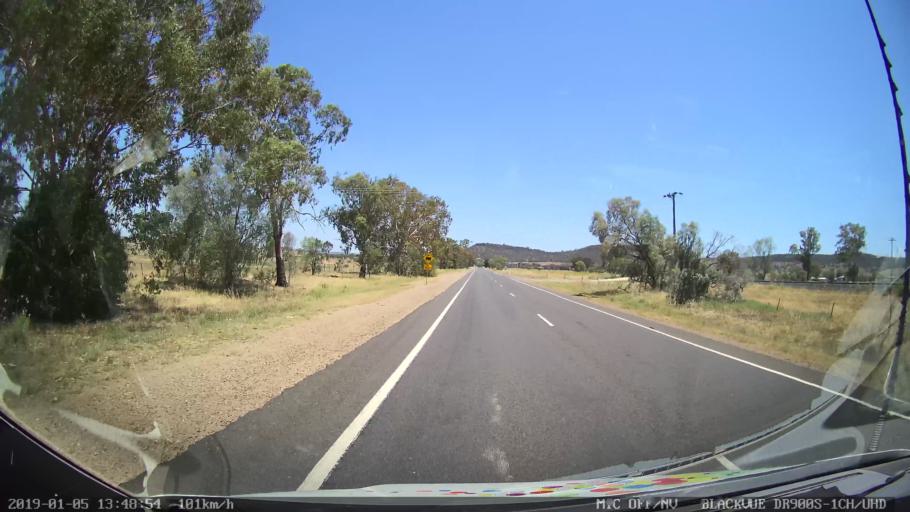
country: AU
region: New South Wales
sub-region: Gunnedah
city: Gunnedah
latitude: -31.0083
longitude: 150.2757
